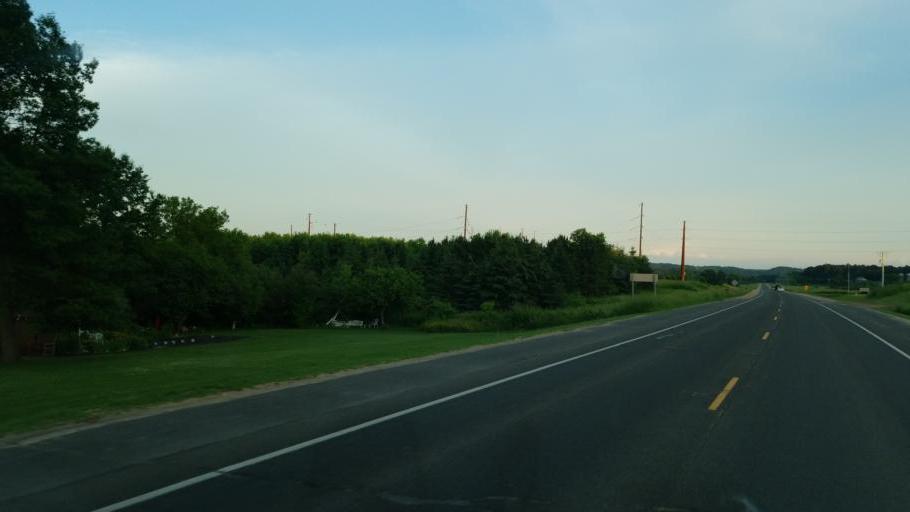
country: US
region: Wisconsin
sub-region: Monroe County
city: Tomah
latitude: 43.9529
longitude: -90.5047
